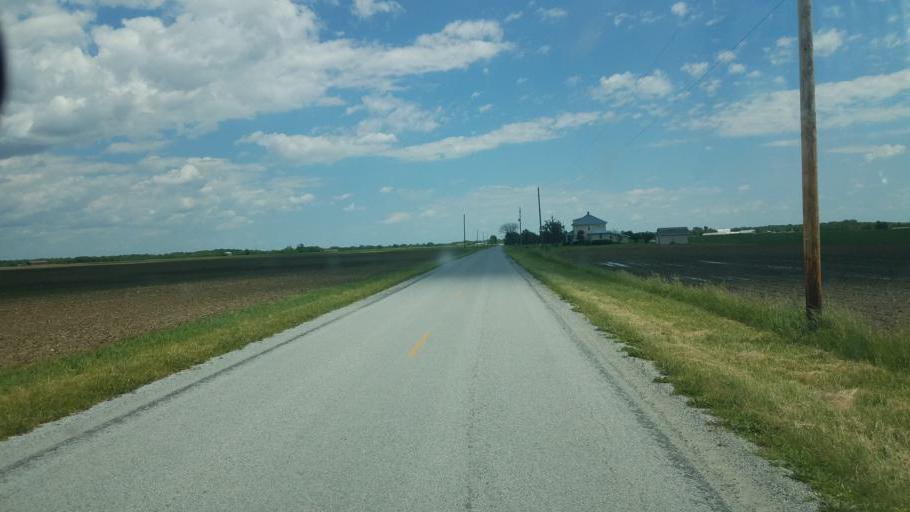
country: US
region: Ohio
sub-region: Hardin County
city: Forest
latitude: 40.6764
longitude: -83.4356
